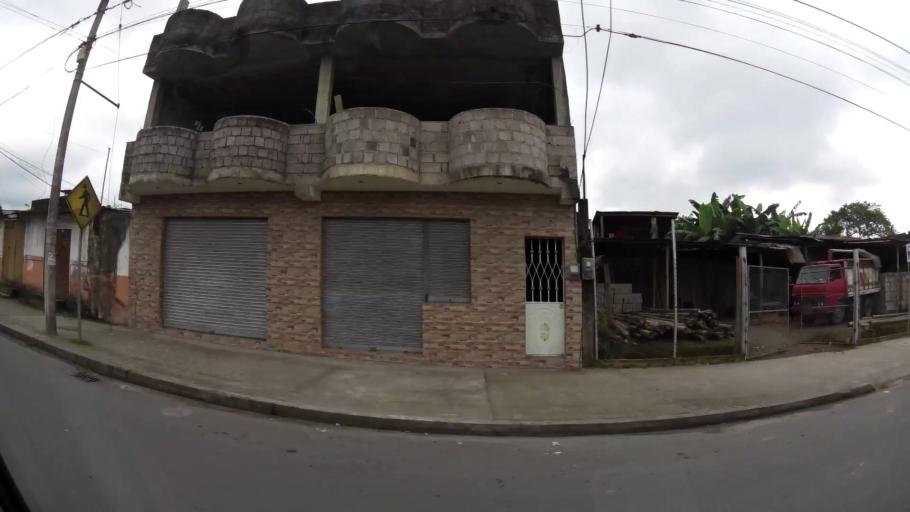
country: EC
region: Santo Domingo de los Tsachilas
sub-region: Canton Santo Domingo de los Colorados
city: Santo Domingo de los Colorados
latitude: -0.2580
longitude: -79.1507
